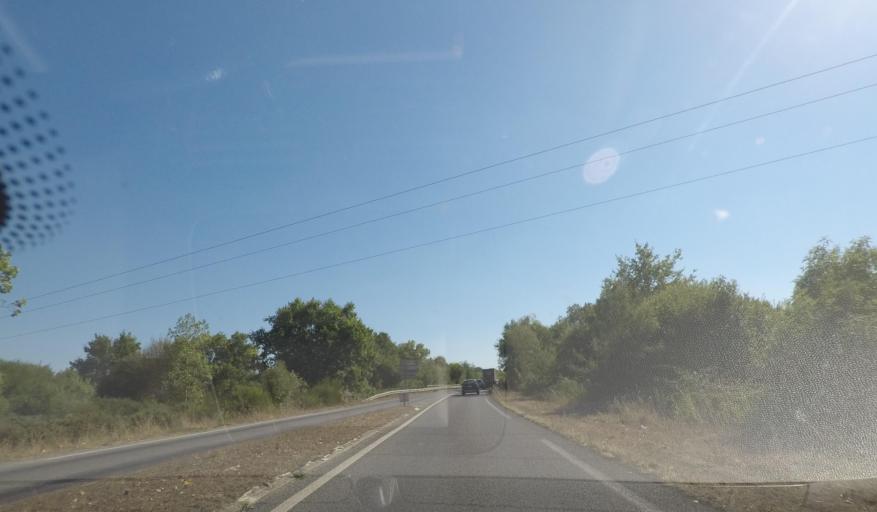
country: FR
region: Pays de la Loire
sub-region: Departement de la Loire-Atlantique
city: Besne
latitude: 47.4112
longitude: -2.0909
